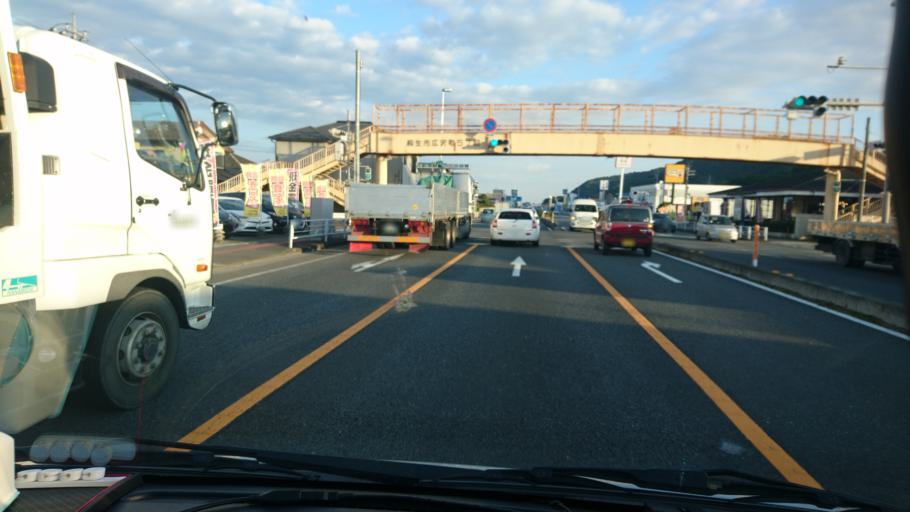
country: JP
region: Gunma
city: Kiryu
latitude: 36.3769
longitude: 139.3467
